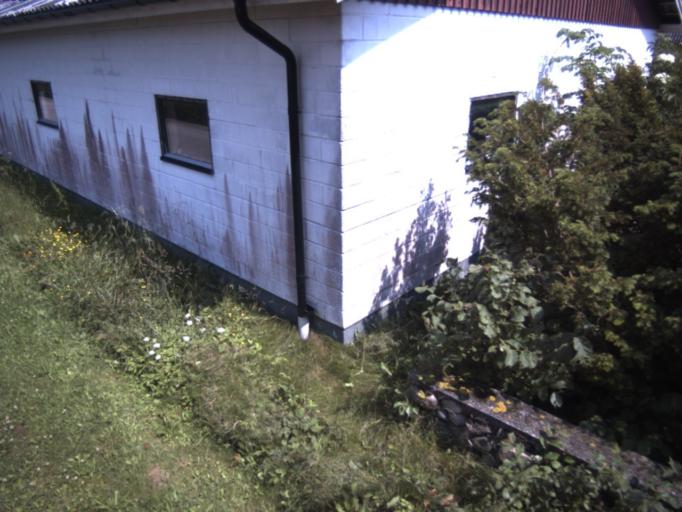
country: SE
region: Skane
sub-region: Angelholms Kommun
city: Strovelstorp
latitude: 56.1438
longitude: 12.7681
